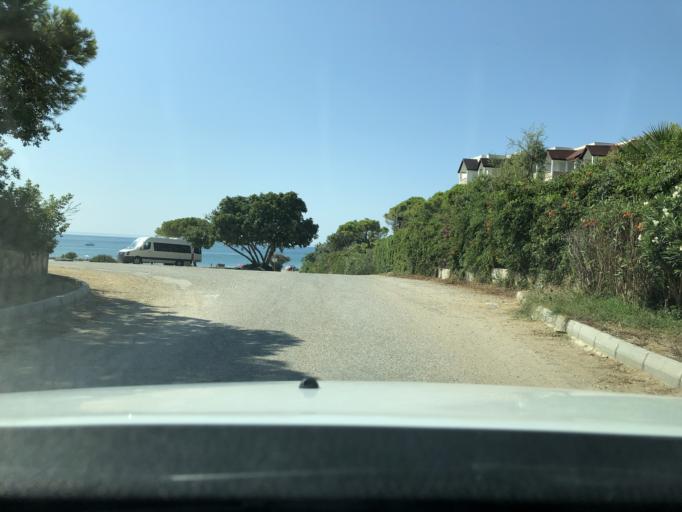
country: TR
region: Antalya
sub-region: Manavgat
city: Manavgat
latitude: 36.7580
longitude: 31.4229
